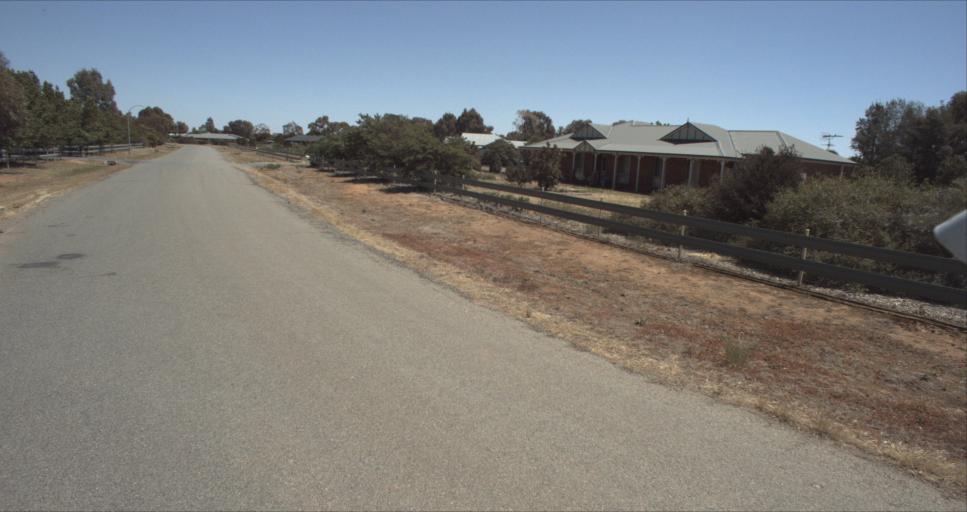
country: AU
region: New South Wales
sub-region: Leeton
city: Leeton
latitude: -34.5297
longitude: 146.3983
